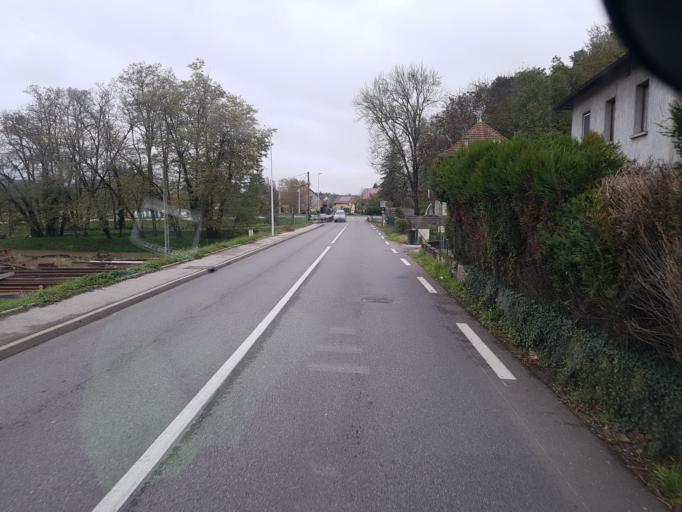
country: FR
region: Rhone-Alpes
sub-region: Departement de la Savoie
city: Saint-Genix-sur-Guiers
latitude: 45.6037
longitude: 5.6405
